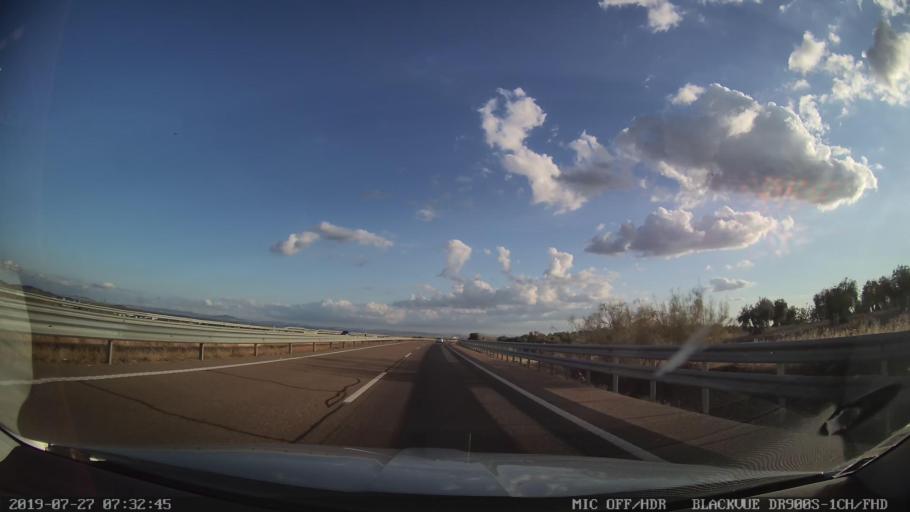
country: ES
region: Extremadura
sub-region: Provincia de Caceres
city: Miajadas
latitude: 39.1535
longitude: -5.9265
